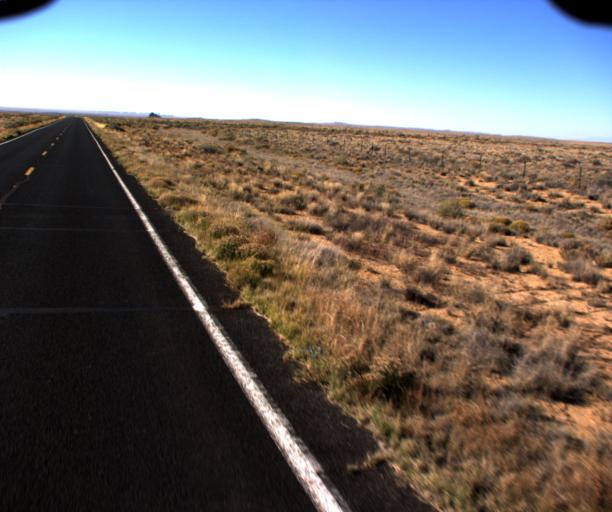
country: US
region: Arizona
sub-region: Navajo County
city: First Mesa
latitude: 35.7502
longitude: -110.5154
